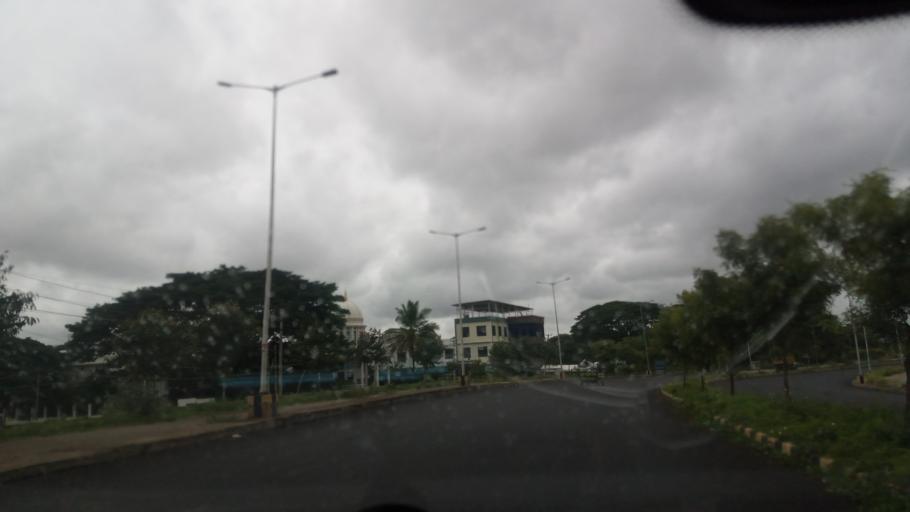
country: IN
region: Karnataka
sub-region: Mysore
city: Mysore
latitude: 12.2850
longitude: 76.6095
